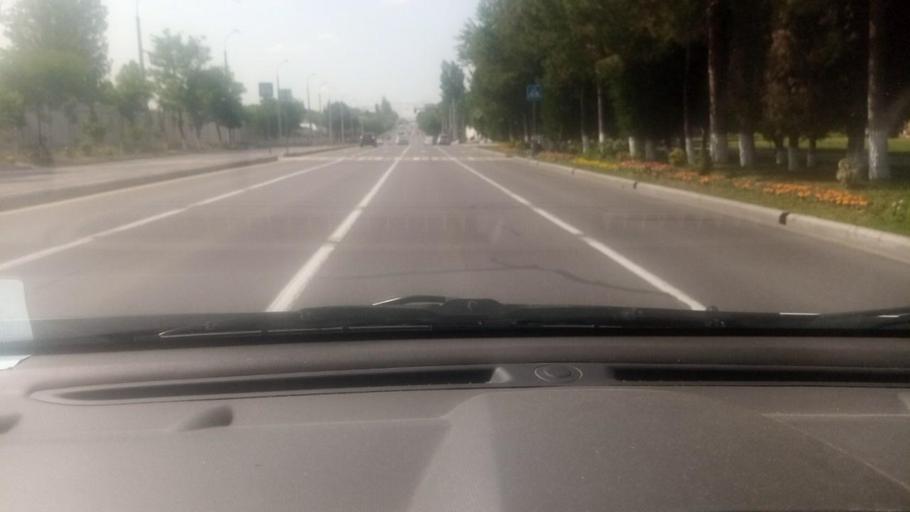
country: UZ
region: Toshkent
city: Salor
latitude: 41.3259
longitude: 69.3601
